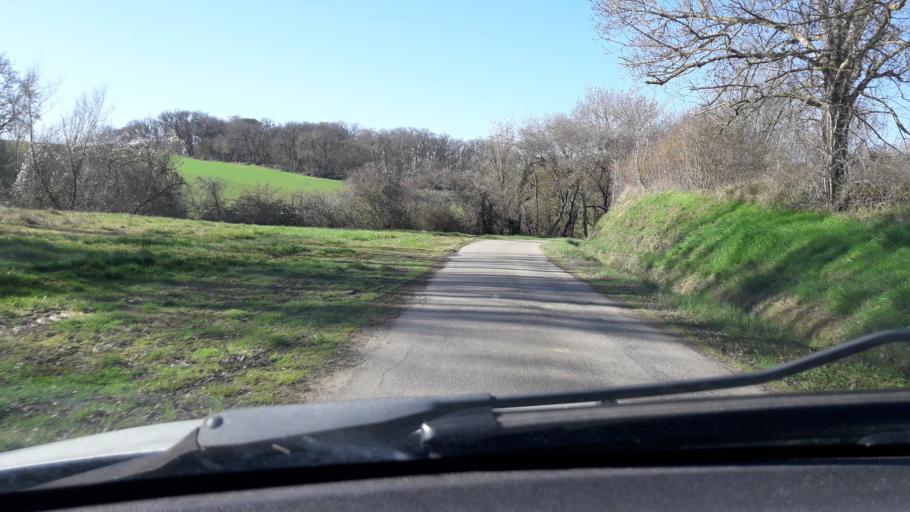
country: FR
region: Midi-Pyrenees
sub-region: Departement du Gers
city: Gimont
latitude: 43.6430
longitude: 1.0116
